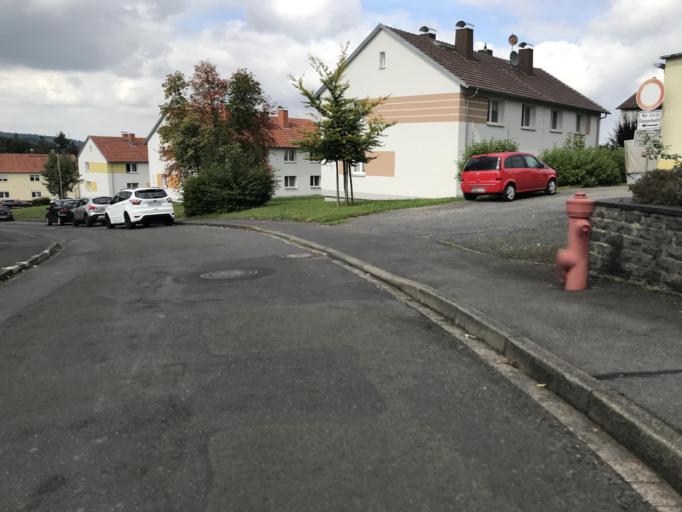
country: DE
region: Hesse
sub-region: Regierungsbezirk Giessen
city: Lauterbach
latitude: 50.6271
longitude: 9.3978
